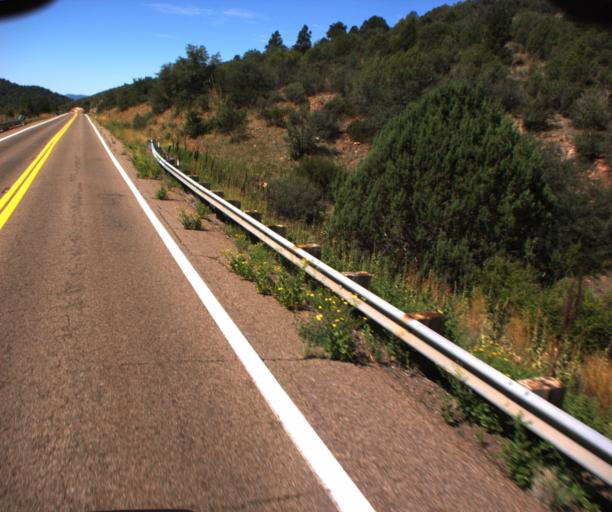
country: US
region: Arizona
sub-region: Navajo County
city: Cibecue
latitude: 33.8822
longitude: -110.3915
